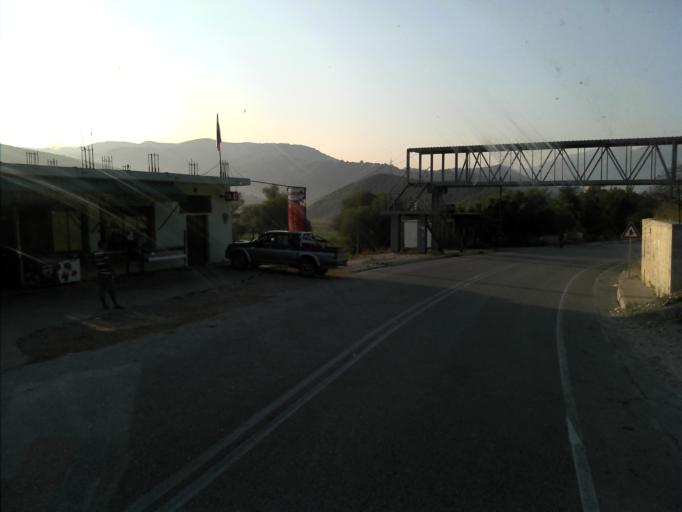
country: AL
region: Gjirokaster
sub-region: Rrethi i Tepelenes
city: Krahes
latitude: 40.4311
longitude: 19.8528
